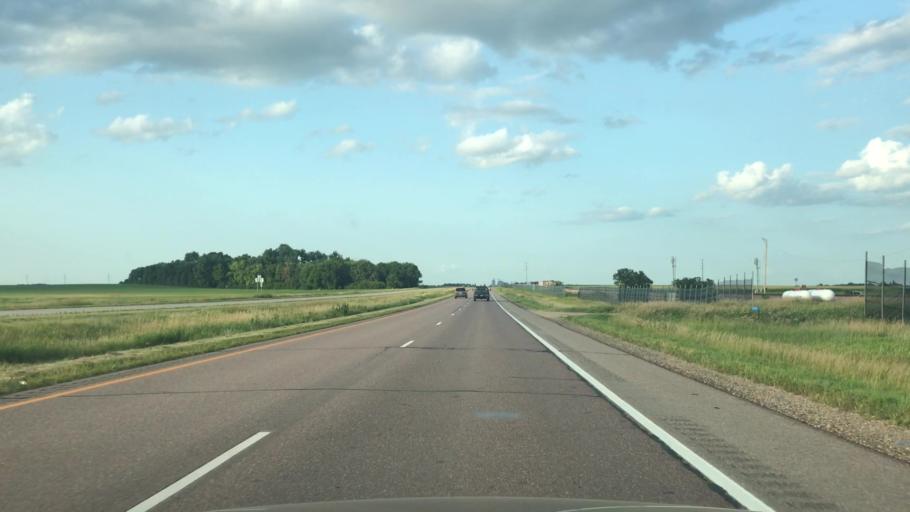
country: US
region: Minnesota
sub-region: Nobles County
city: Worthington
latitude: 43.6626
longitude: -95.5269
